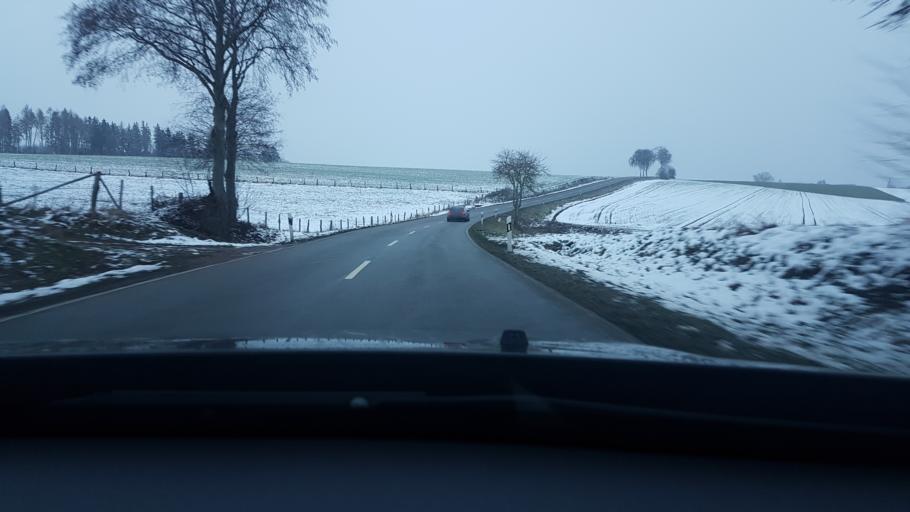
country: DE
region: North Rhine-Westphalia
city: Marsberg
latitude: 51.3814
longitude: 8.8731
